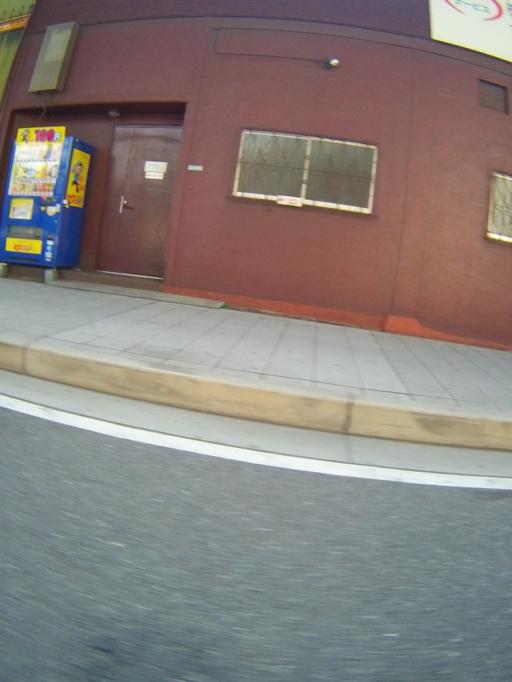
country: JP
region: Osaka
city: Osaka-shi
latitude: 34.6598
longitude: 135.4672
